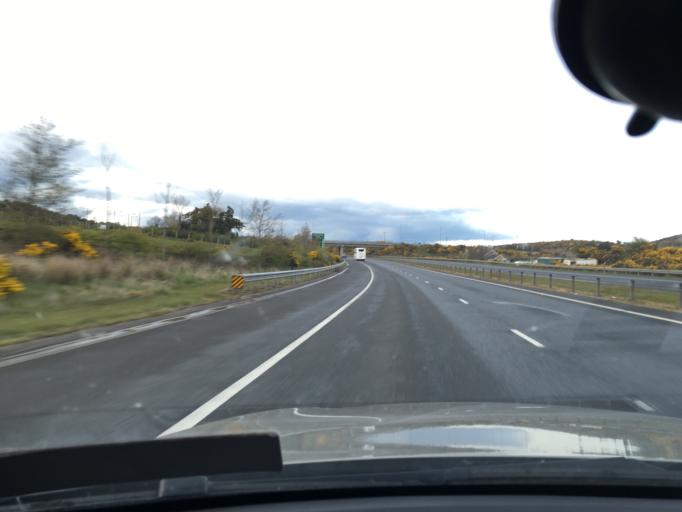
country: GB
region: Northern Ireland
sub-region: Newry and Mourne District
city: Newry
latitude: 54.1358
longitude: -6.3464
